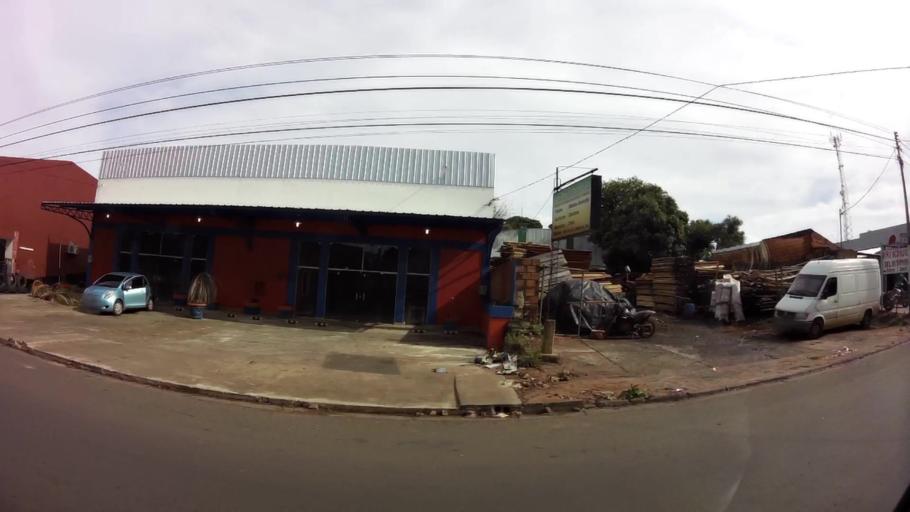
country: PY
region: Central
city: Limpio
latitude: -25.1676
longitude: -57.4722
